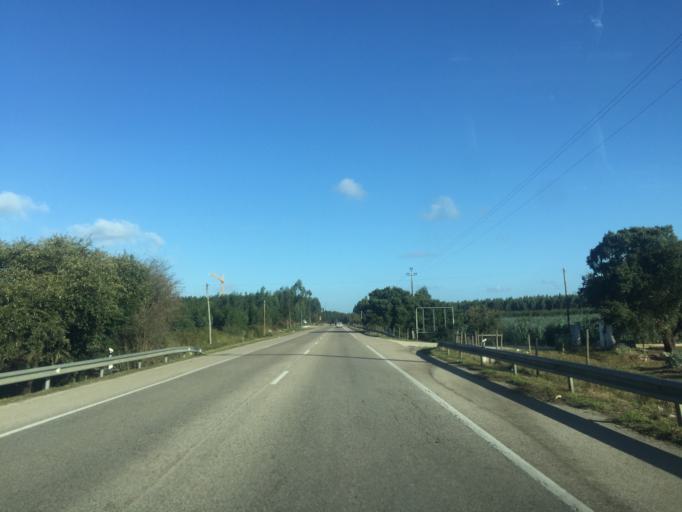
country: PT
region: Leiria
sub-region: Alcobaca
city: Benedita
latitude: 39.4118
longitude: -8.9625
